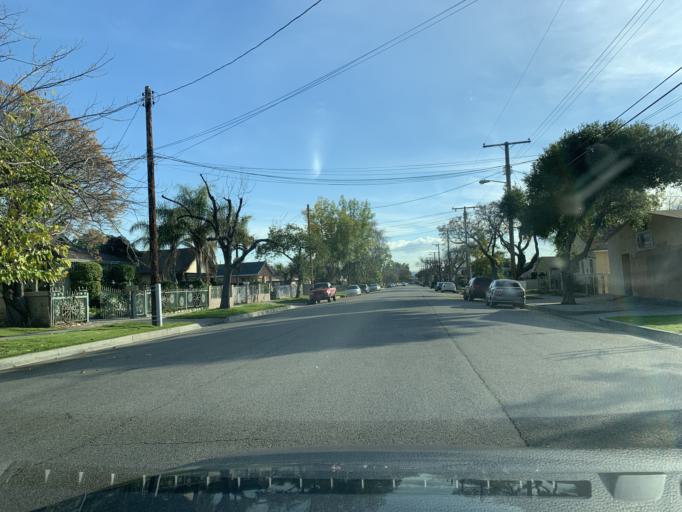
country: US
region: California
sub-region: Los Angeles County
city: Azusa
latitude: 34.1258
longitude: -117.9037
